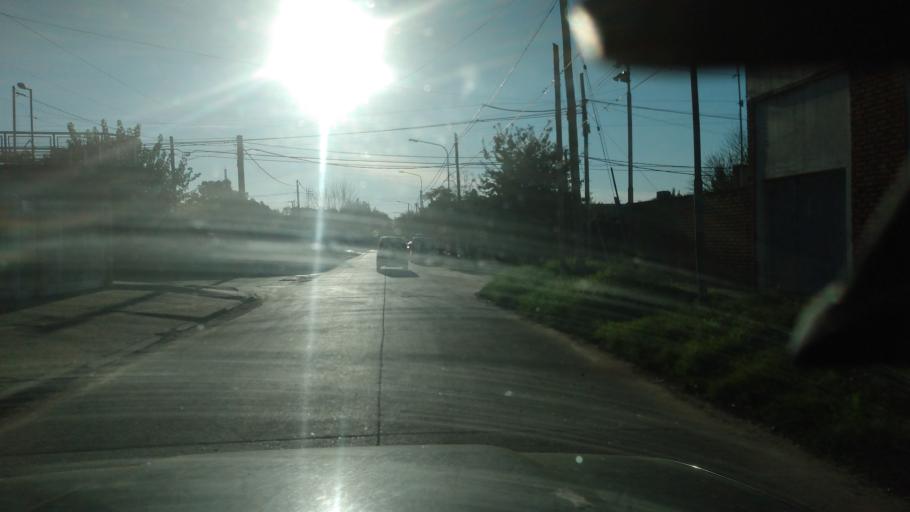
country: AR
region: Buenos Aires
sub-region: Partido de Lujan
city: Lujan
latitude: -34.5694
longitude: -59.0931
